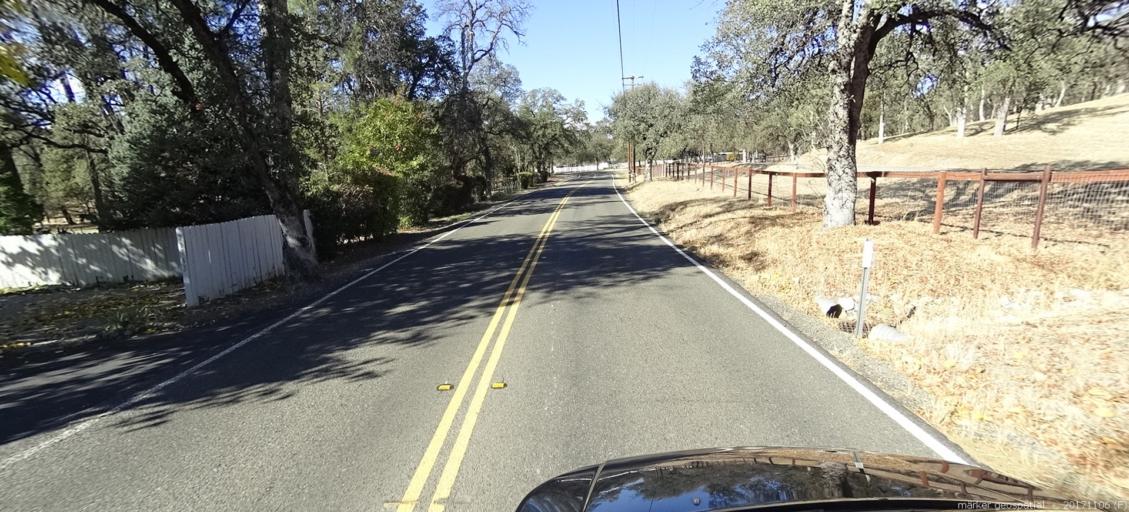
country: US
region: California
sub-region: Shasta County
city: Palo Cedro
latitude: 40.5916
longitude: -122.2477
